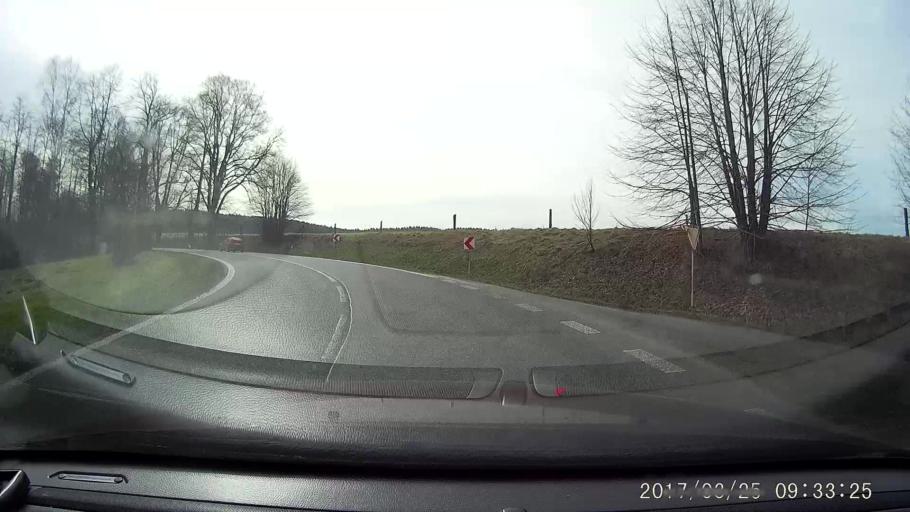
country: PL
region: Silesian Voivodeship
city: Zawidow
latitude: 50.9779
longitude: 15.0760
